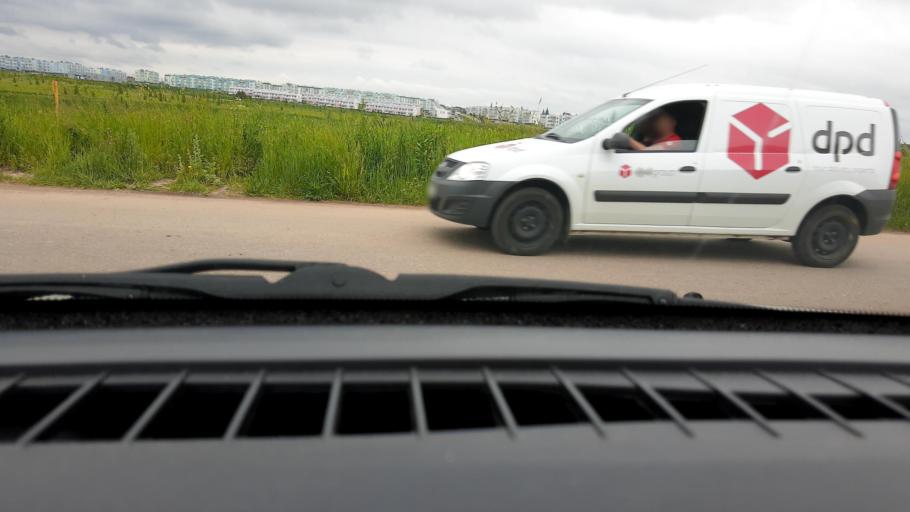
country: RU
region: Nizjnij Novgorod
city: Burevestnik
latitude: 56.1853
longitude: 43.8511
